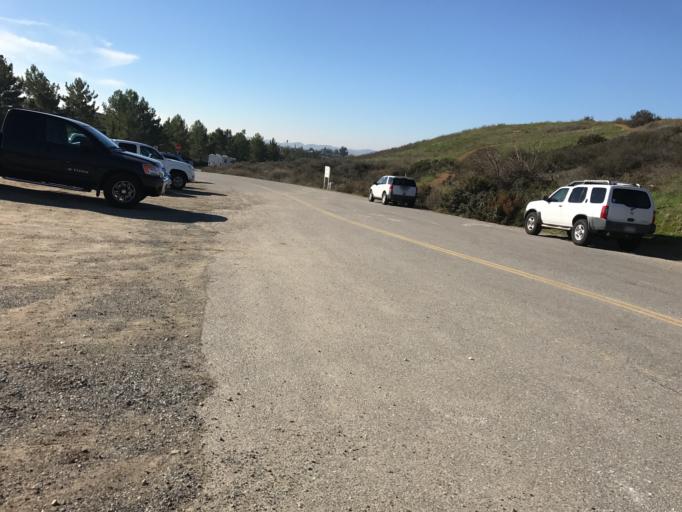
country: US
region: California
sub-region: San Bernardino County
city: Yucaipa
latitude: 34.0431
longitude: -117.0586
